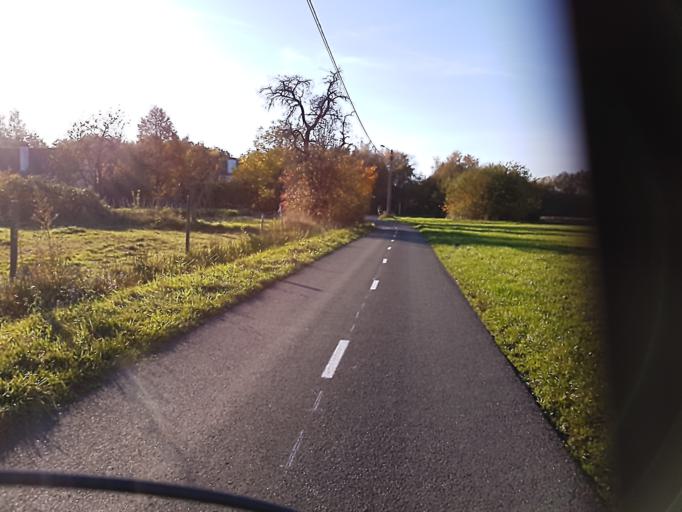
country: BE
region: Flanders
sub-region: Provincie Antwerpen
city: Bonheiden
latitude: 51.0415
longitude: 4.5462
